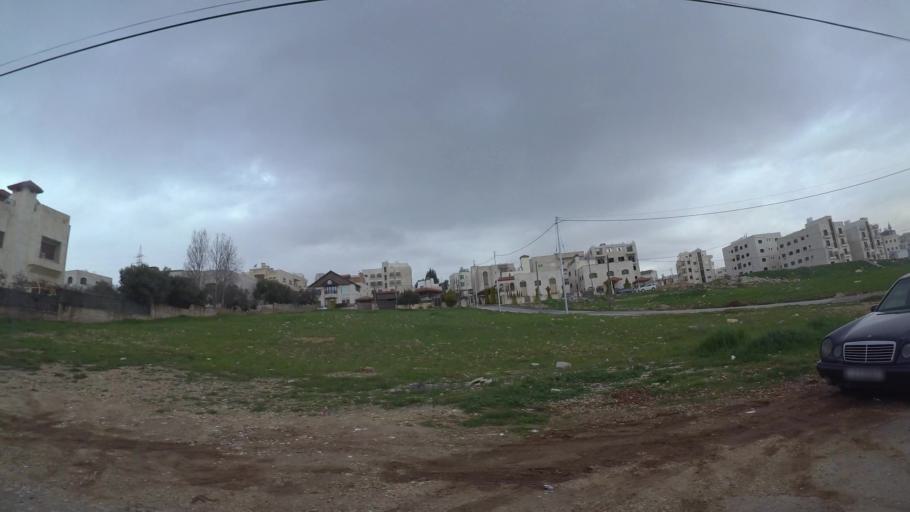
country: JO
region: Amman
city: Umm as Summaq
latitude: 31.9018
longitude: 35.8342
